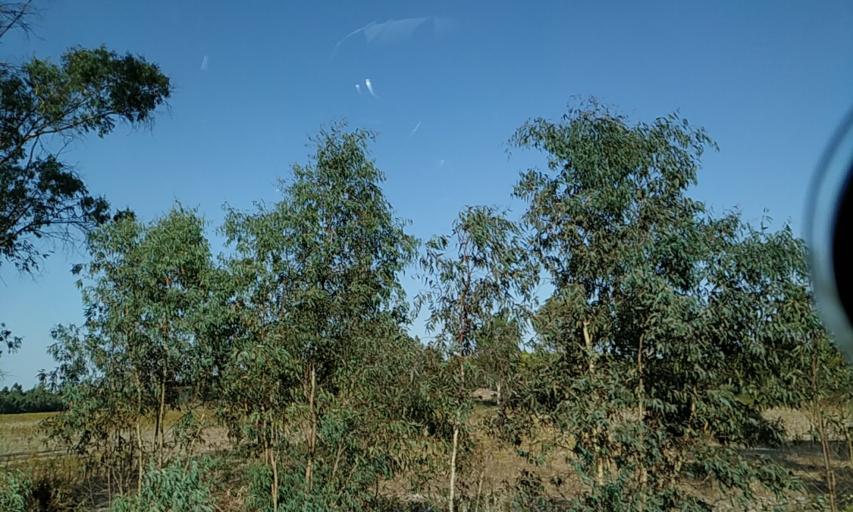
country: PT
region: Santarem
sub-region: Coruche
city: Coruche
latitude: 39.0142
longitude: -8.5627
